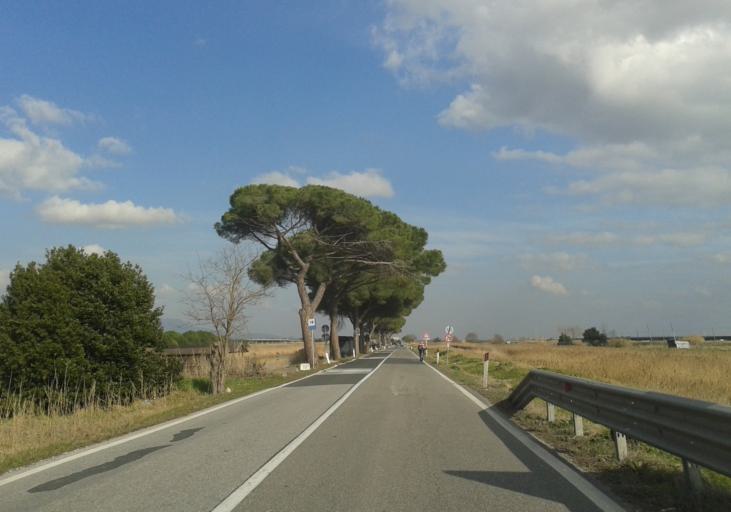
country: IT
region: Tuscany
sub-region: Provincia di Livorno
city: Guasticce
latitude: 43.6025
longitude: 10.3608
